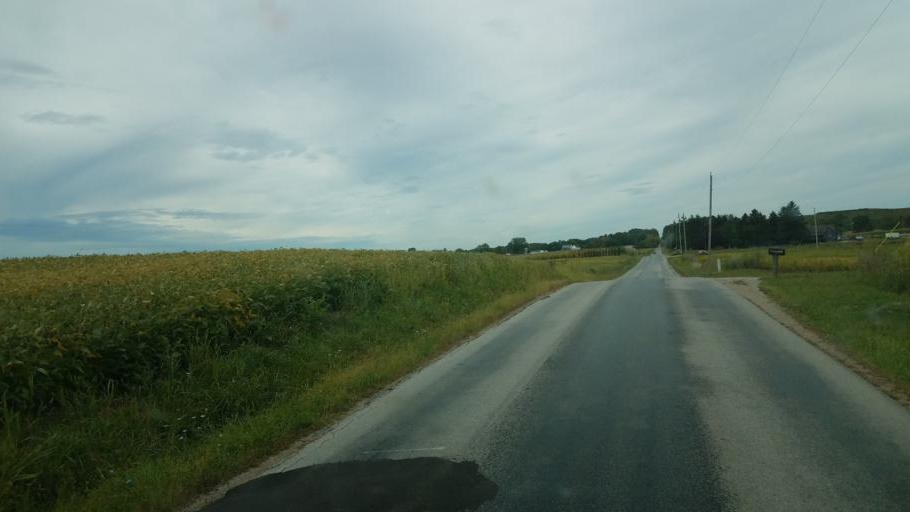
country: US
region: Ohio
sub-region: Knox County
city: Centerburg
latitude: 40.3207
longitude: -82.7078
